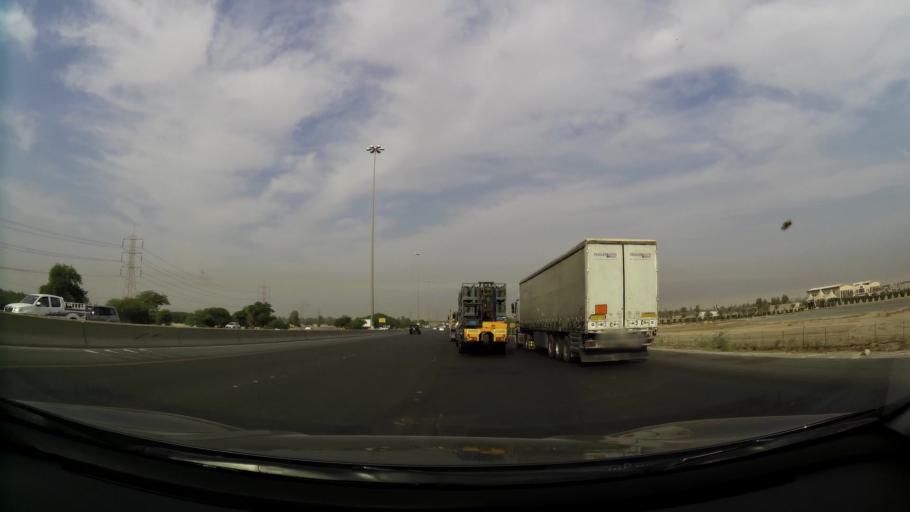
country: KW
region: Al Asimah
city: Ar Rabiyah
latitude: 29.2773
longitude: 47.8033
